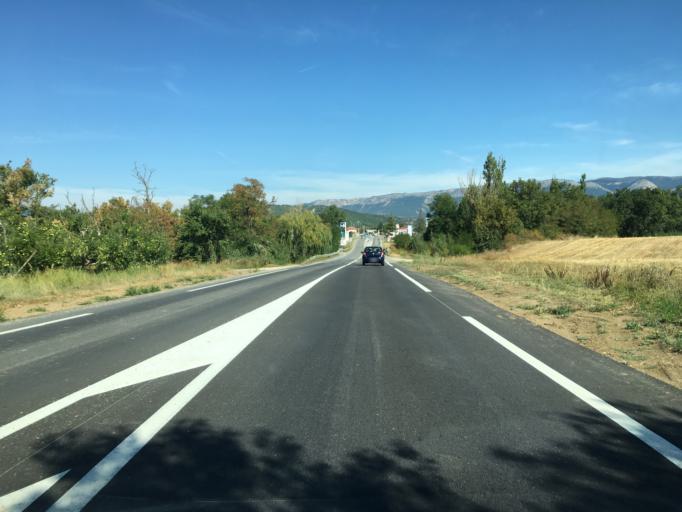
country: FR
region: Provence-Alpes-Cote d'Azur
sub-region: Departement des Hautes-Alpes
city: Laragne-Monteglin
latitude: 44.3008
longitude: 5.8385
